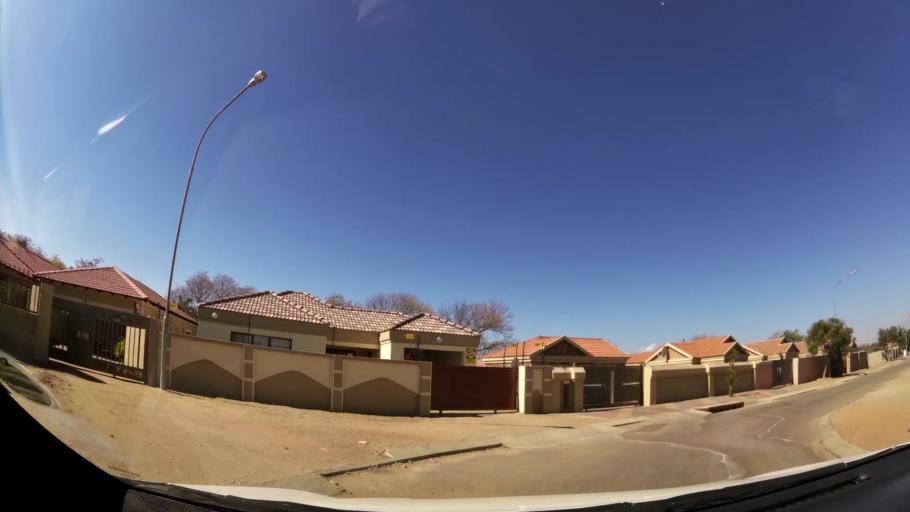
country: ZA
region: Limpopo
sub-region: Capricorn District Municipality
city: Polokwane
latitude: -23.8595
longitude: 29.4262
